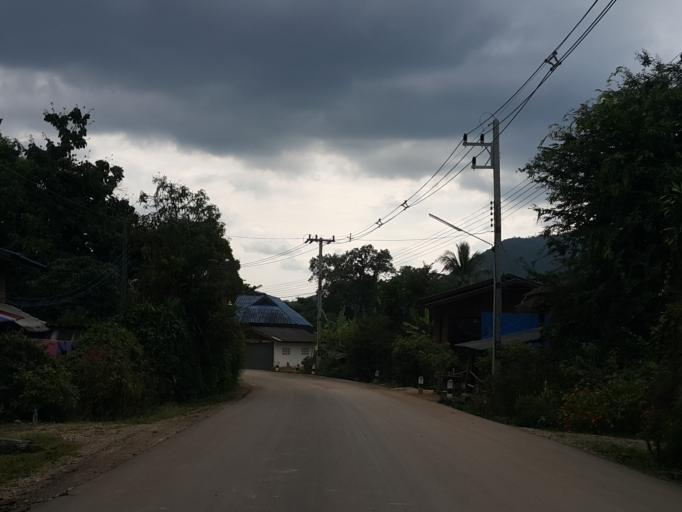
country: TH
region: Lampang
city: Chae Hom
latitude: 18.5757
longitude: 99.4538
